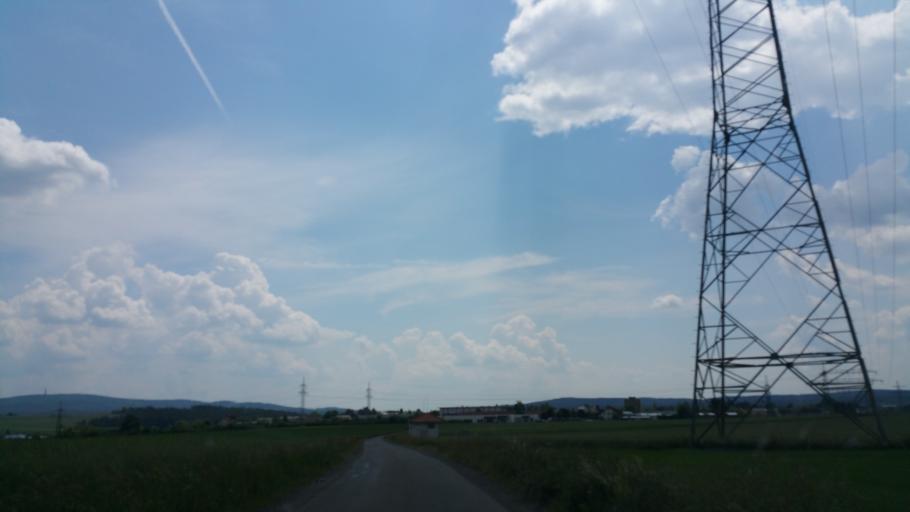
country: DE
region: Bavaria
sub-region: Upper Franconia
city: Schwarzenbach an der Saale
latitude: 50.2300
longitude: 11.9462
